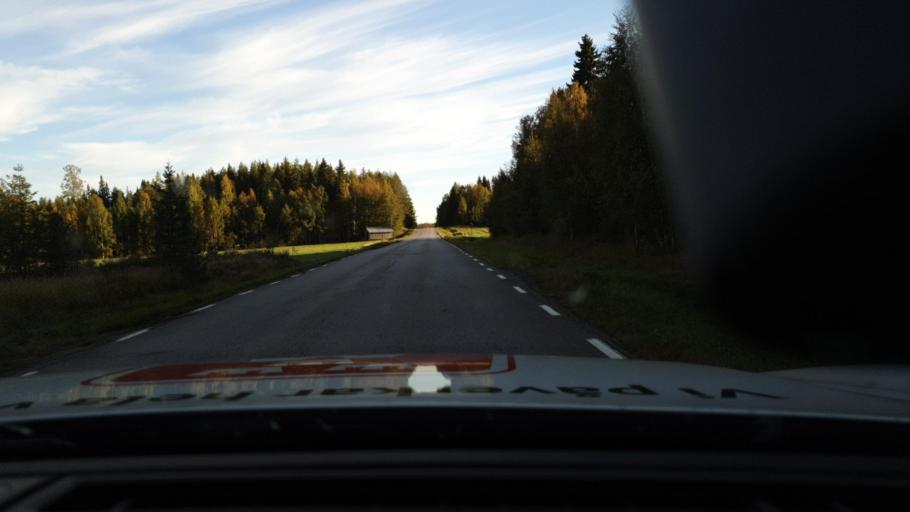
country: SE
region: Norrbotten
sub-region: Kalix Kommun
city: Toere
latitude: 65.8668
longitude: 22.6768
